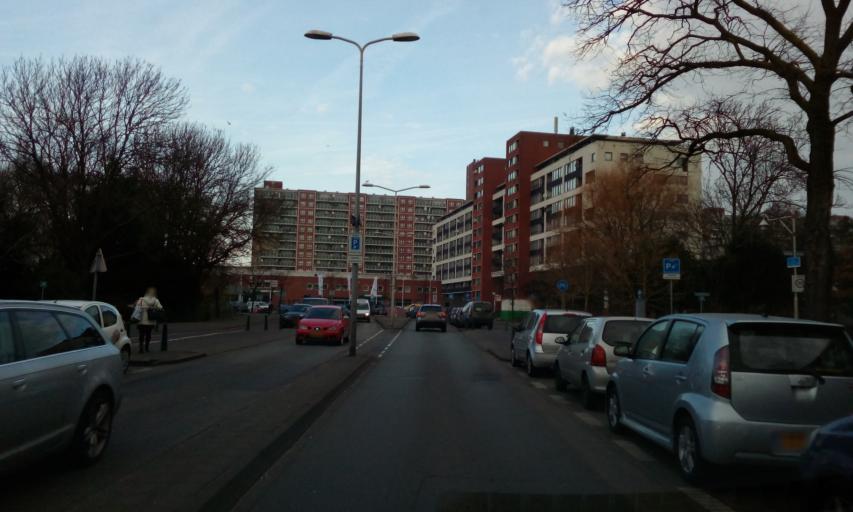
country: NL
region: South Holland
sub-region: Gemeente Rijswijk
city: Rijswijk
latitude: 52.0602
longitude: 4.3199
